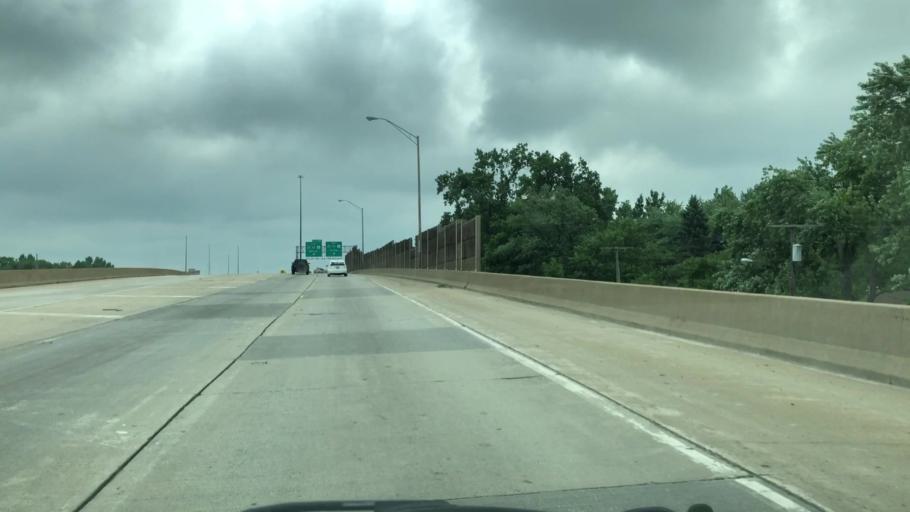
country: US
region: Indiana
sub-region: Lake County
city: Highland
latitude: 41.5764
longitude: -87.4330
